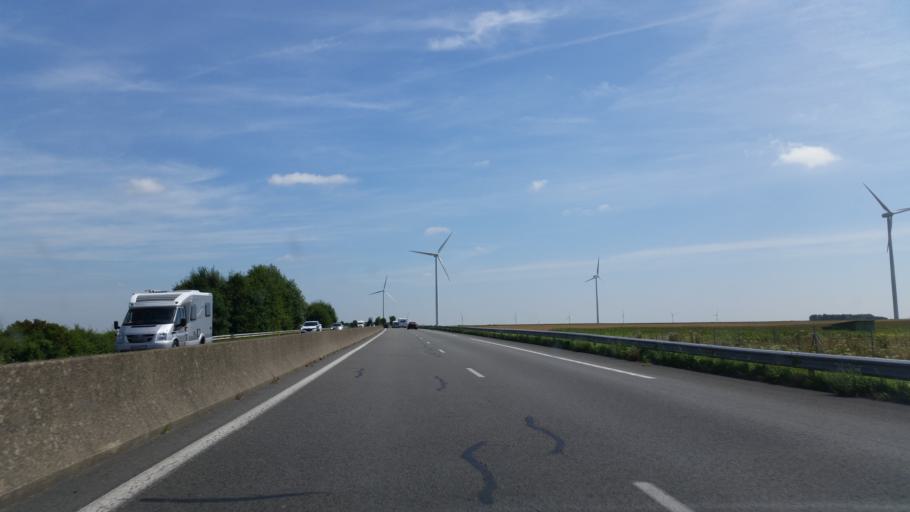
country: FR
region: Picardie
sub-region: Departement de la Somme
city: Rosieres-en-Santerre
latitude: 49.8532
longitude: 2.7371
